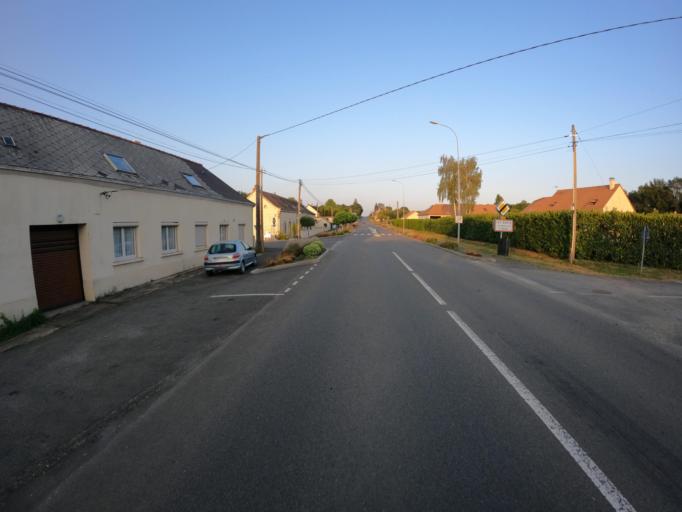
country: FR
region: Pays de la Loire
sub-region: Departement de la Sarthe
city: Auvers-le-Hamon
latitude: 47.8674
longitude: -0.4289
